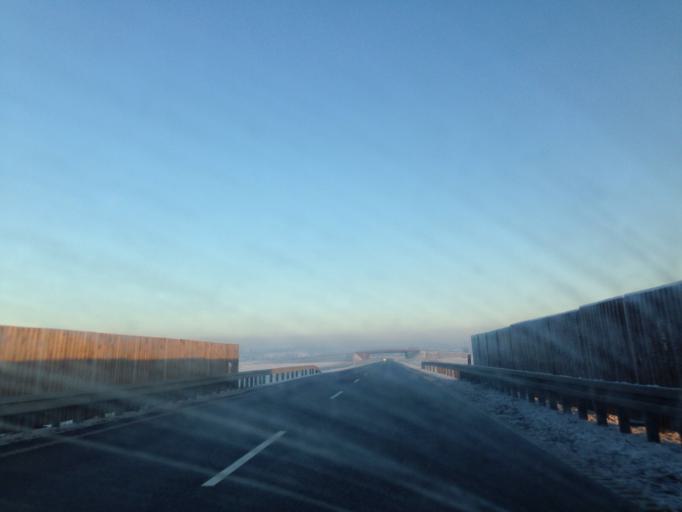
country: PL
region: Pomeranian Voivodeship
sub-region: Powiat kwidzynski
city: Kwidzyn
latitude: 53.7572
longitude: 18.8885
